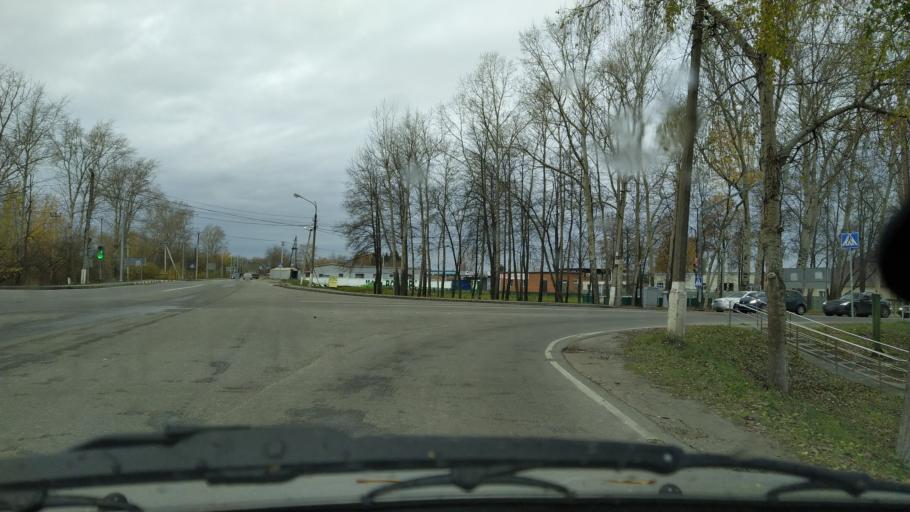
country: RU
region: Moskovskaya
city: Voskresensk
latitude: 55.3169
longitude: 38.6484
